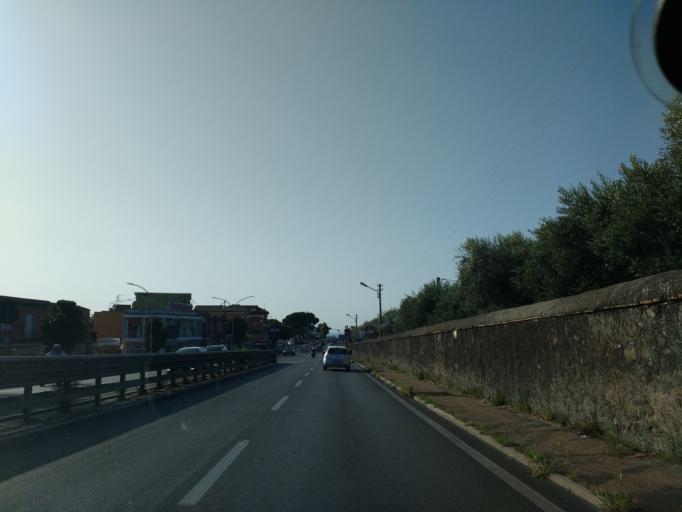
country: IT
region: Latium
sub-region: Citta metropolitana di Roma Capitale
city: Marino
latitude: 41.7648
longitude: 12.6187
